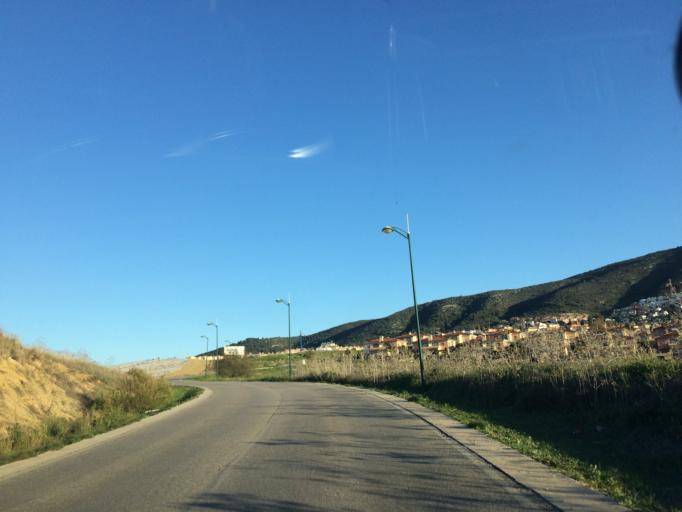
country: ES
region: Andalusia
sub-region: Provincia de Malaga
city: Alhaurin de la Torre
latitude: 36.6691
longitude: -4.5376
